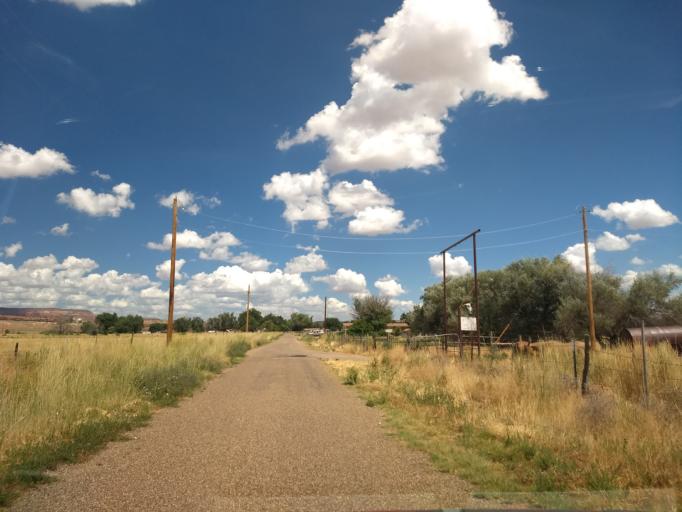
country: US
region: Arizona
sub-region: Coconino County
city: Fredonia
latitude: 36.9413
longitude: -112.5308
